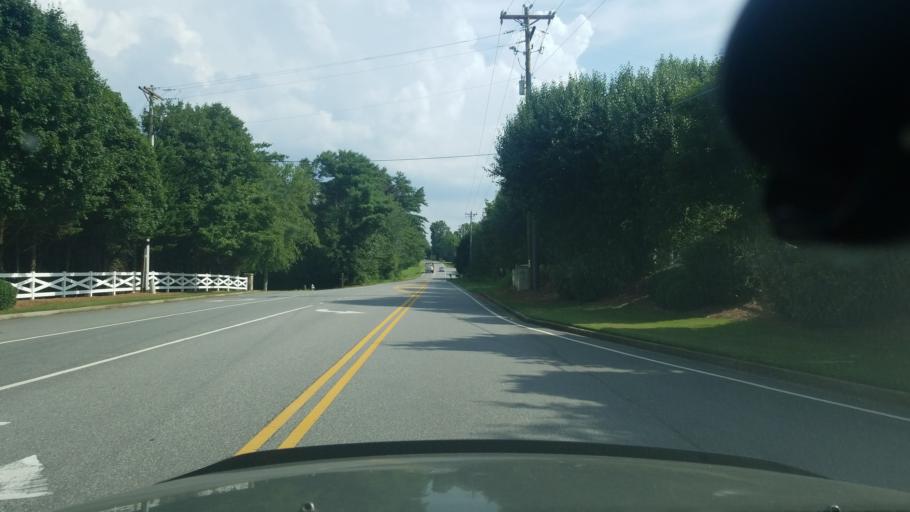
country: US
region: Georgia
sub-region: Hall County
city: Flowery Branch
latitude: 34.2774
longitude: -84.0009
